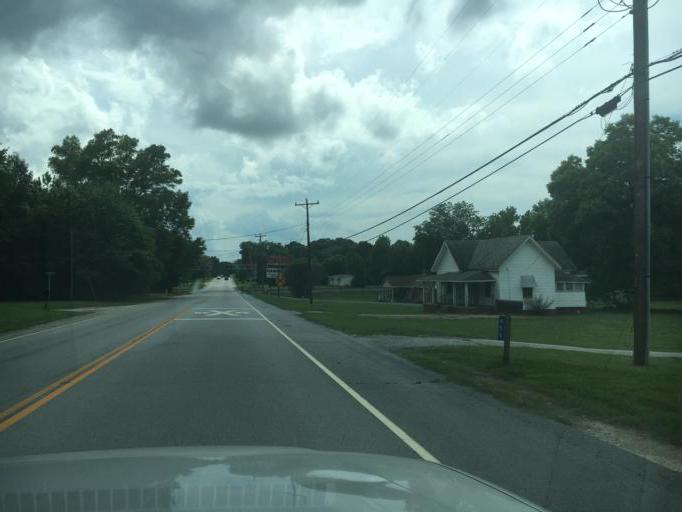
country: US
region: South Carolina
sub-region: Laurens County
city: Watts Mills
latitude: 34.5266
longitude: -81.9879
